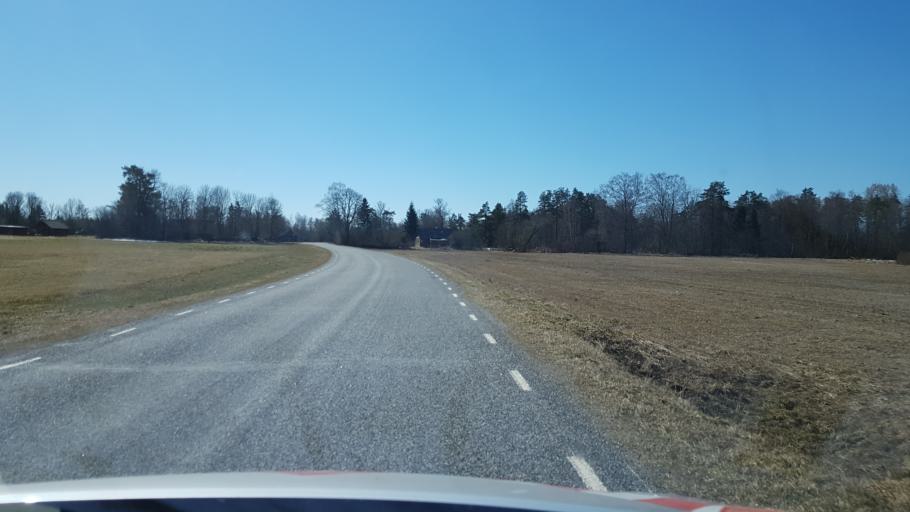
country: EE
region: Laeaene-Virumaa
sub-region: Haljala vald
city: Haljala
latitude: 59.4692
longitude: 26.2425
